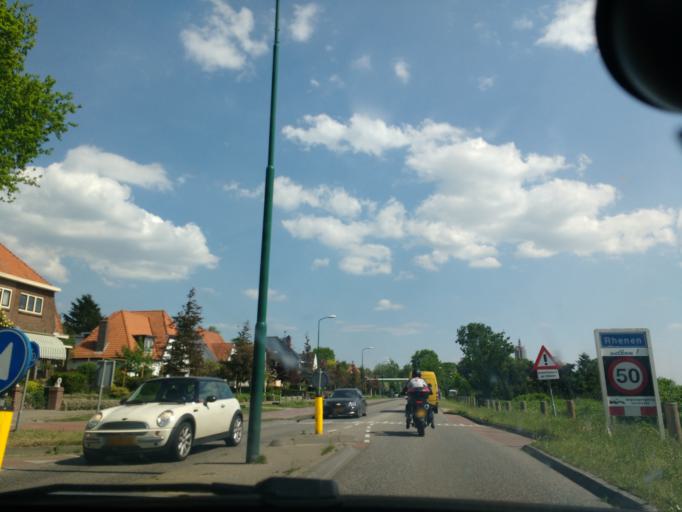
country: NL
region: Utrecht
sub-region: Gemeente Rhenen
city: Rhenen
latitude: 51.9619
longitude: 5.5562
